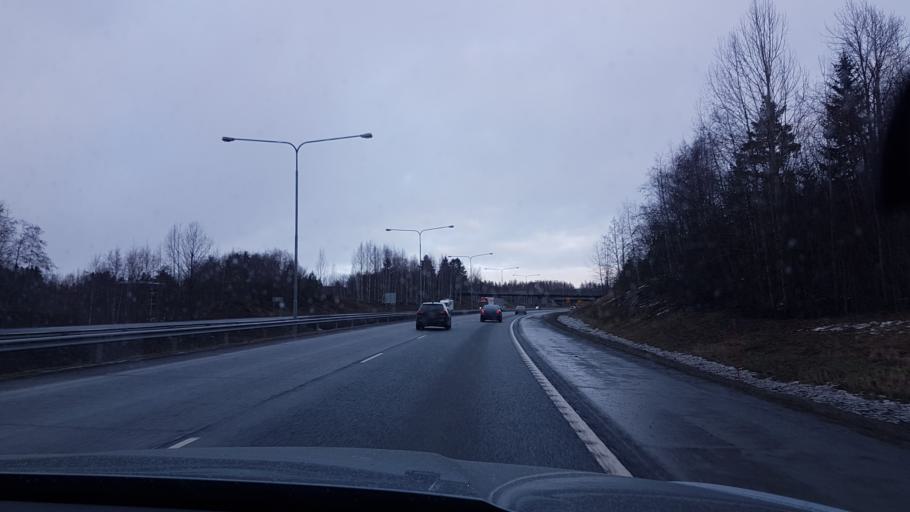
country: FI
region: Pirkanmaa
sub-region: Tampere
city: Tampere
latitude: 61.4930
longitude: 23.8763
